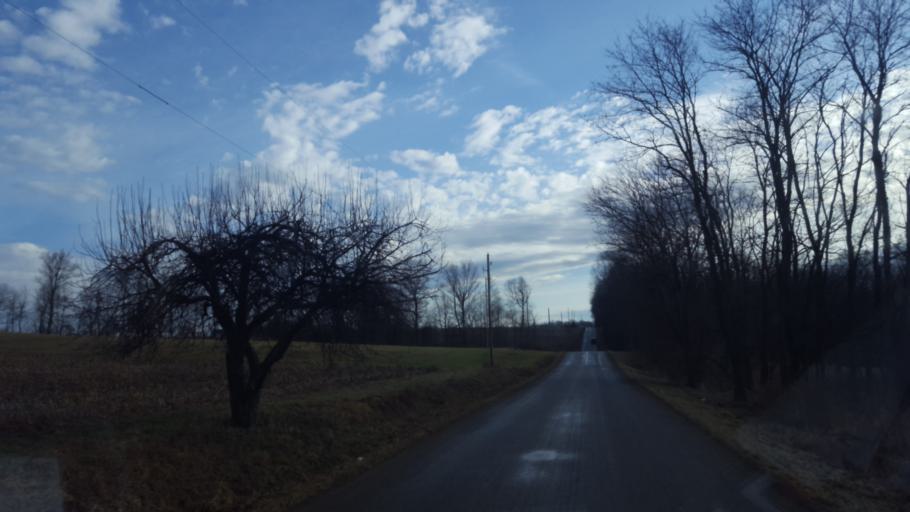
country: US
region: Ohio
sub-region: Richland County
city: Lexington
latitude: 40.6446
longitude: -82.5835
